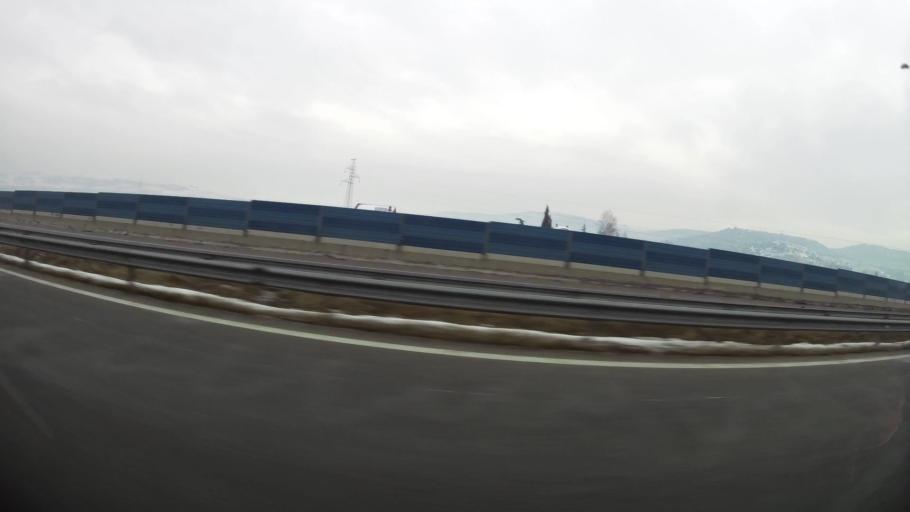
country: MK
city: Kondovo
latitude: 42.0326
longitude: 21.3318
